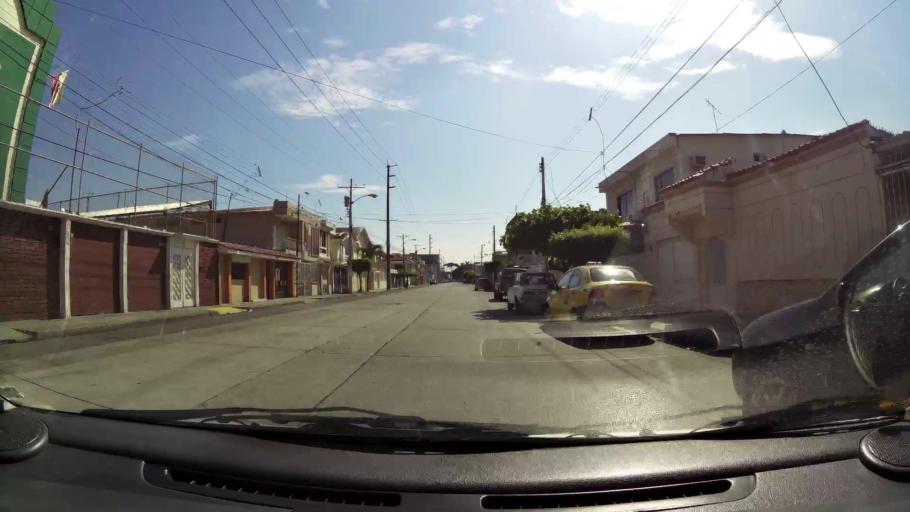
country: EC
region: Guayas
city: Guayaquil
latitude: -2.2285
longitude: -79.8948
